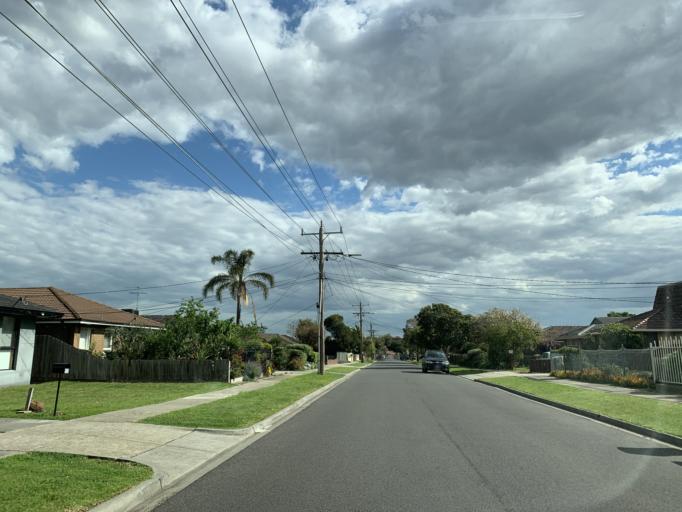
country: AU
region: Victoria
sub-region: Moonee Valley
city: Keilor East
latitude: -37.7420
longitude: 144.8522
